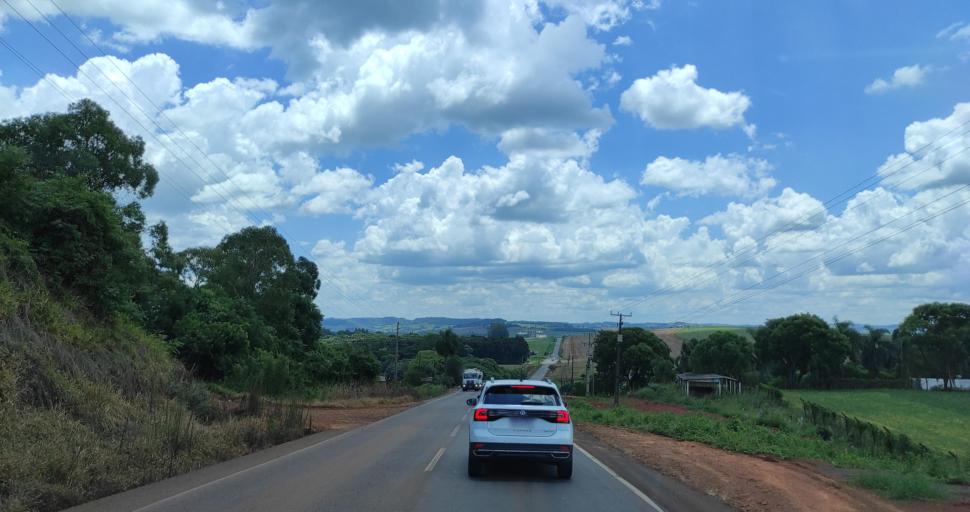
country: BR
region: Santa Catarina
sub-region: Xanxere
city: Xanxere
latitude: -26.7757
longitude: -52.4067
